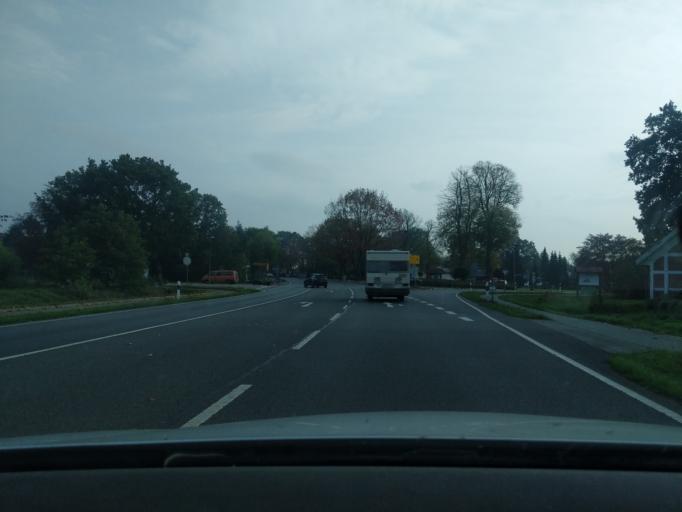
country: DE
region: Lower Saxony
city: Burweg
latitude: 53.6251
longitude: 9.2632
